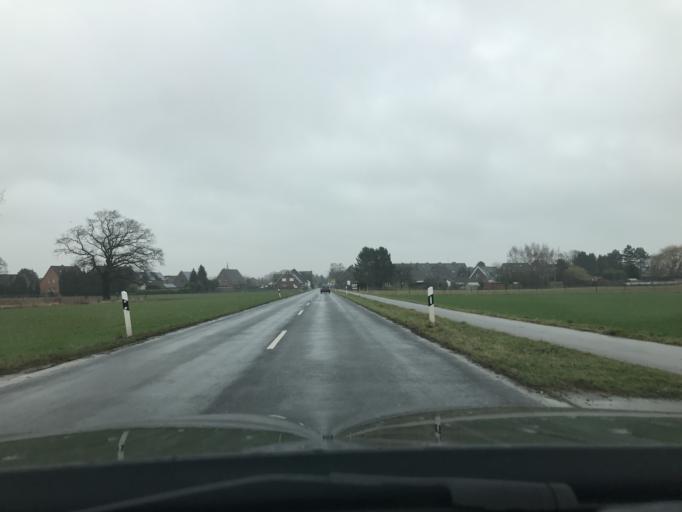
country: DE
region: North Rhine-Westphalia
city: Kempen
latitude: 51.3874
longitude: 6.4387
